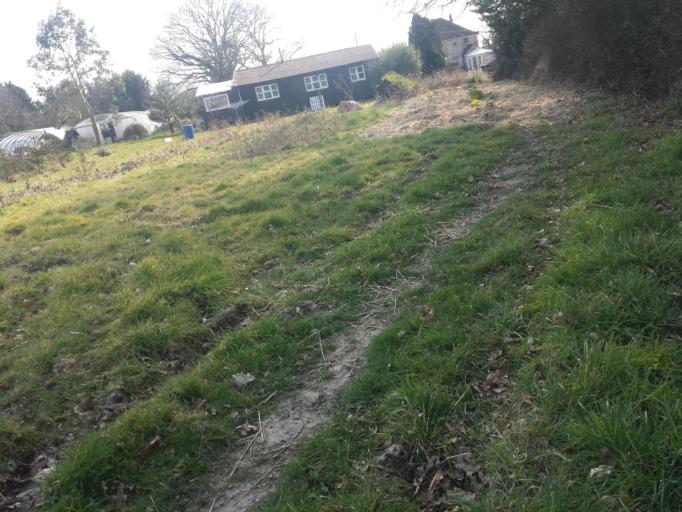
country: GB
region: England
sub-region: Essex
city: Little Clacton
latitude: 51.8826
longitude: 1.1590
